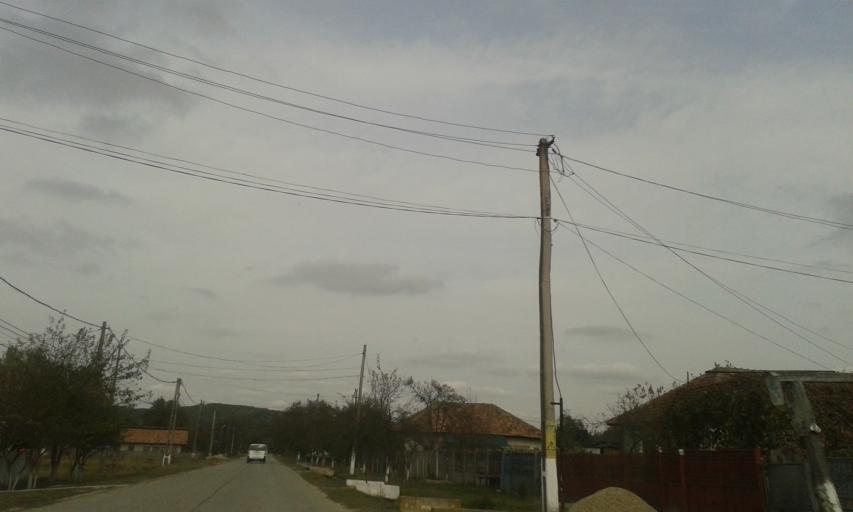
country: RO
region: Gorj
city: Logresti
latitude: 44.8793
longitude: 23.7105
